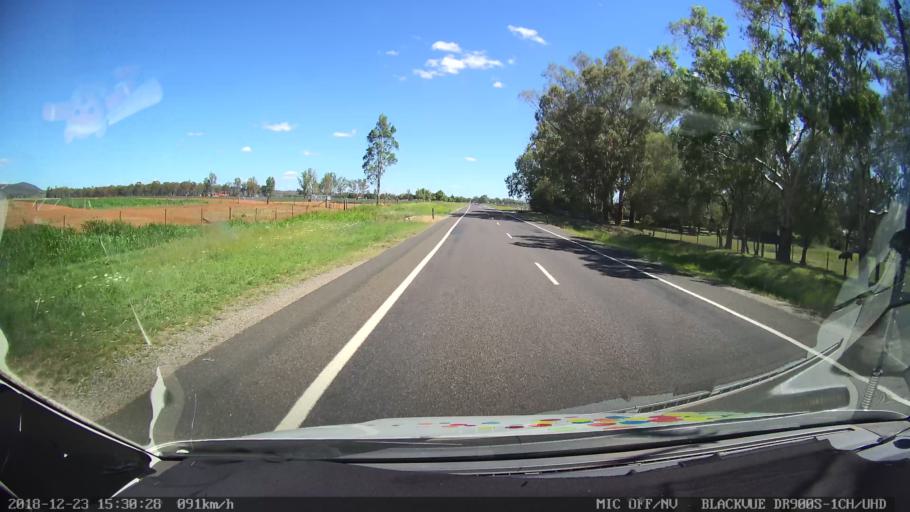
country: AU
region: New South Wales
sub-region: Tamworth Municipality
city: East Tamworth
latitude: -30.9591
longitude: 150.8663
